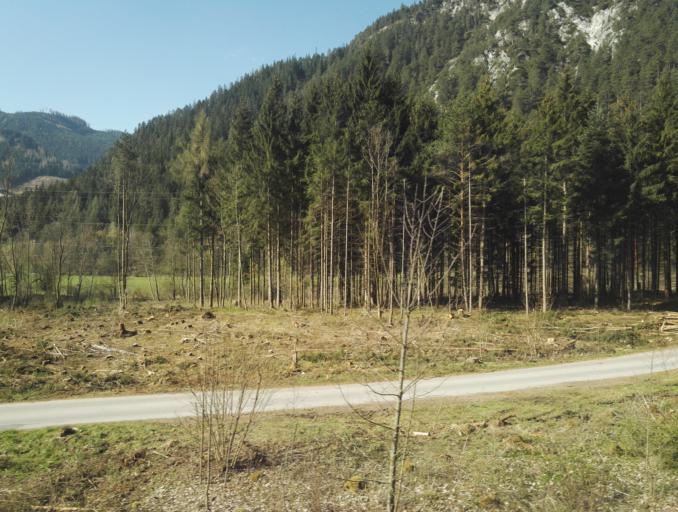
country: AT
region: Salzburg
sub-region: Politischer Bezirk Sankt Johann im Pongau
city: Forstau
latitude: 47.3930
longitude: 13.5927
